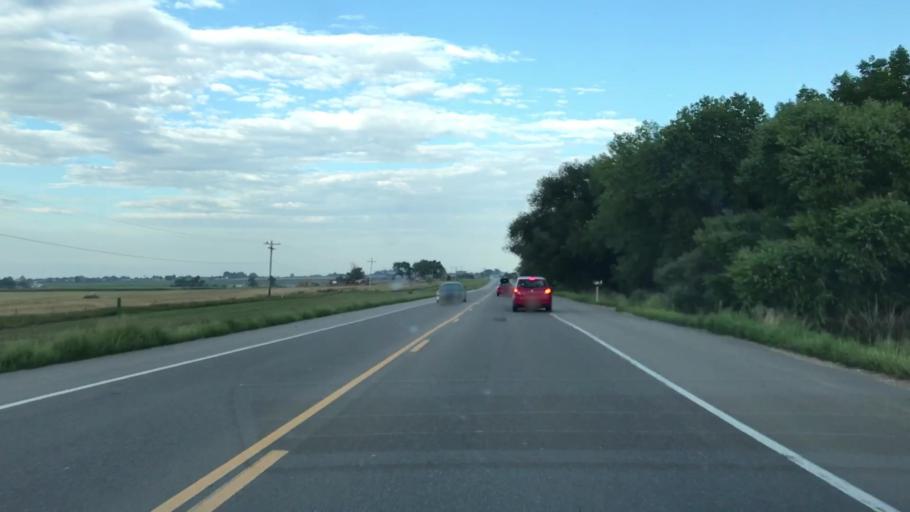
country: US
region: Colorado
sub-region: Weld County
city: Mead
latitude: 40.2039
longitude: -105.0331
